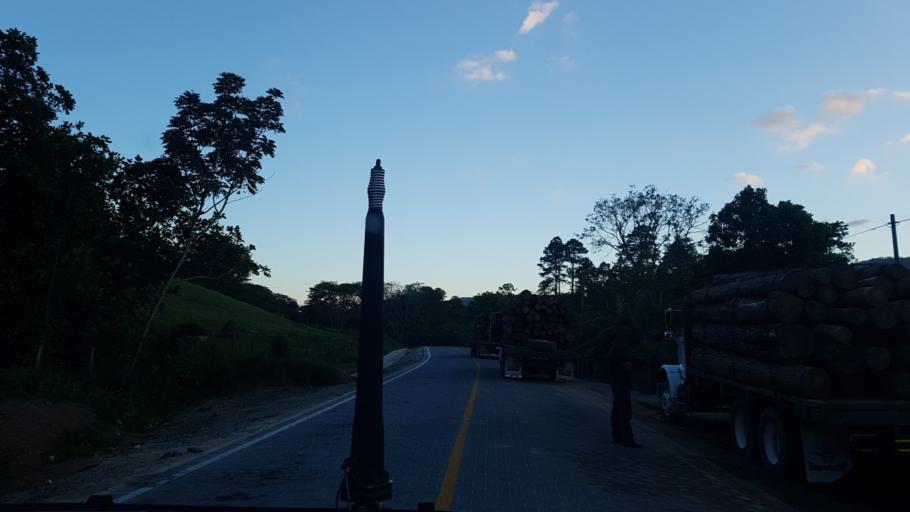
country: NI
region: Nueva Segovia
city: Ocotal
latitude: 13.6799
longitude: -86.6205
